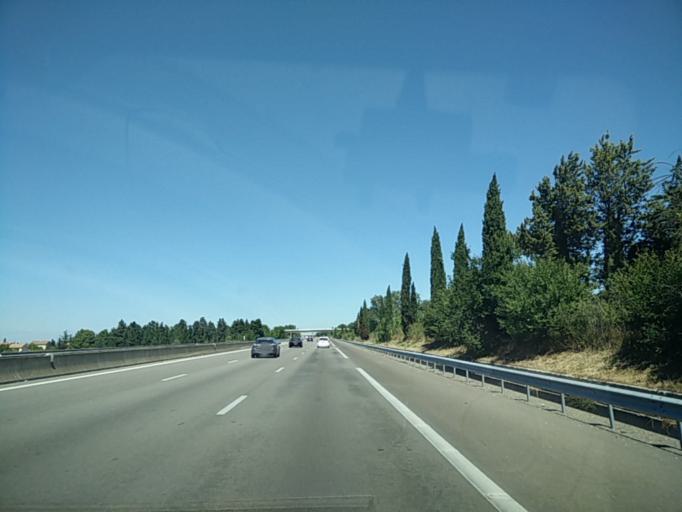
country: FR
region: Provence-Alpes-Cote d'Azur
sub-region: Departement du Vaucluse
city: Morieres-les-Avignon
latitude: 43.9390
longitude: 4.9119
